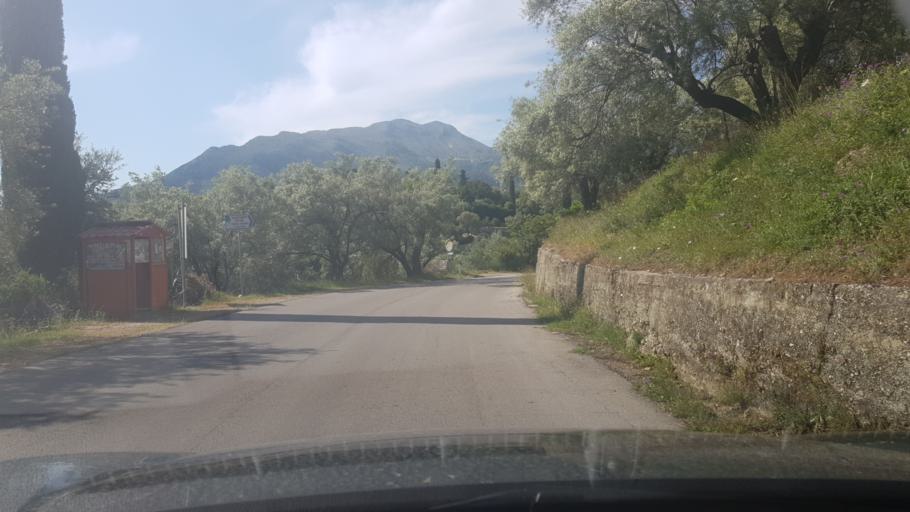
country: GR
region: Ionian Islands
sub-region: Lefkada
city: Nidri
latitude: 38.6598
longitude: 20.6557
